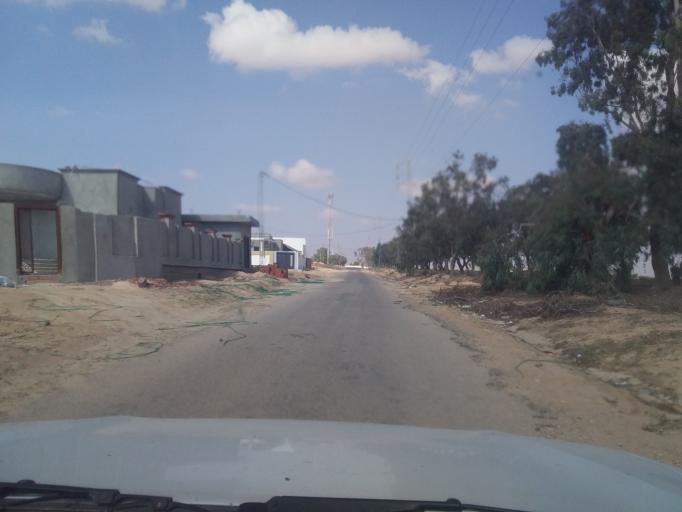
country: TN
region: Qabis
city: Gabes
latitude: 33.6313
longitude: 10.2774
